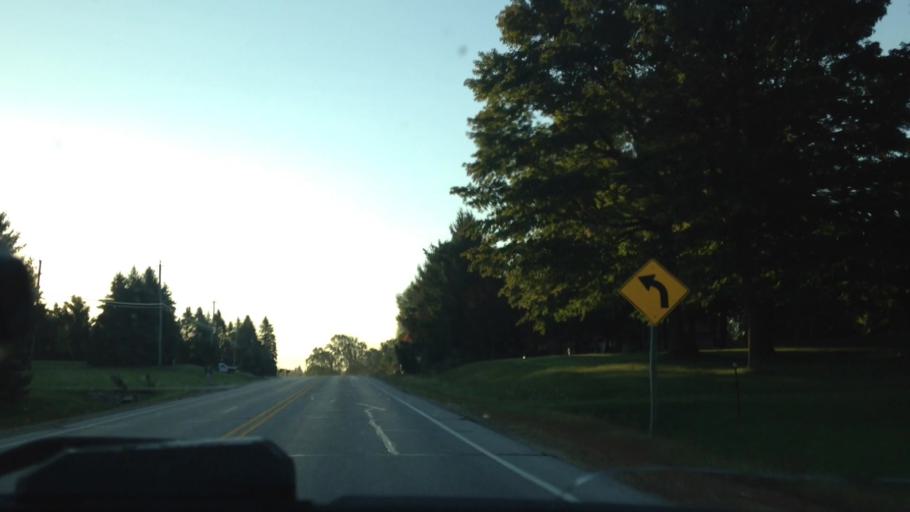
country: US
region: Wisconsin
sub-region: Washington County
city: Newburg
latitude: 43.4245
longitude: -88.0764
